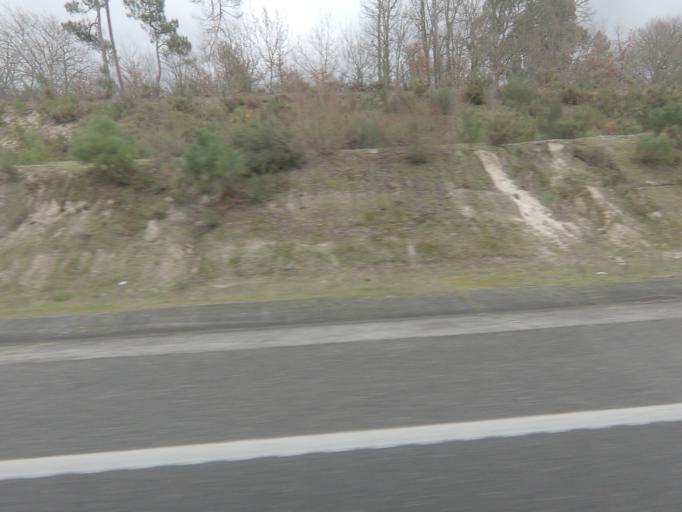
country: ES
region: Galicia
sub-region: Provincia de Ourense
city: Pinor
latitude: 42.4750
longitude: -8.0269
